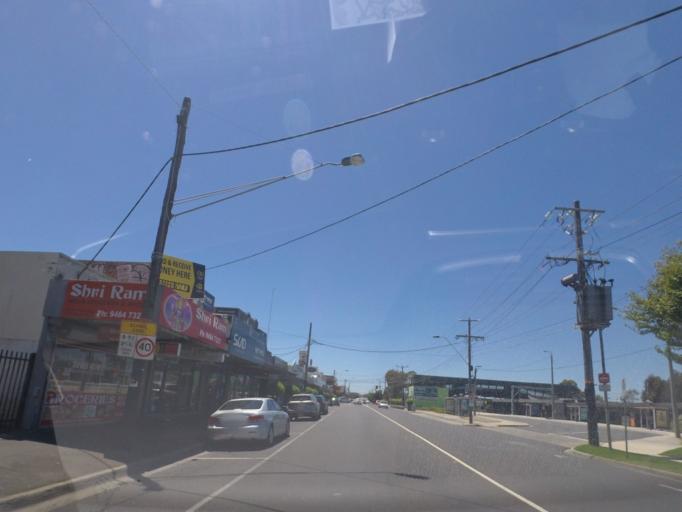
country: AU
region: Victoria
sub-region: Whittlesea
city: Thomastown
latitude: -37.6813
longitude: 145.0136
